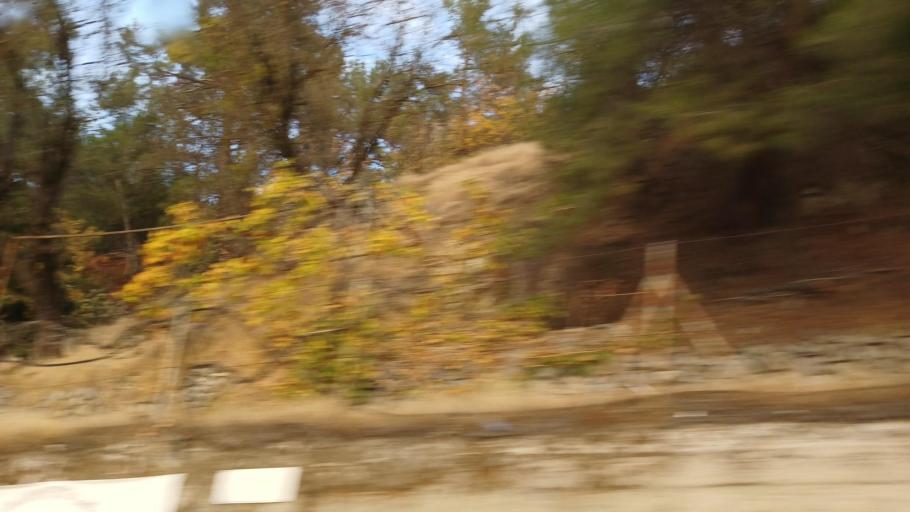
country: CY
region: Lefkosia
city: Kakopetria
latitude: 34.9725
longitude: 32.9195
